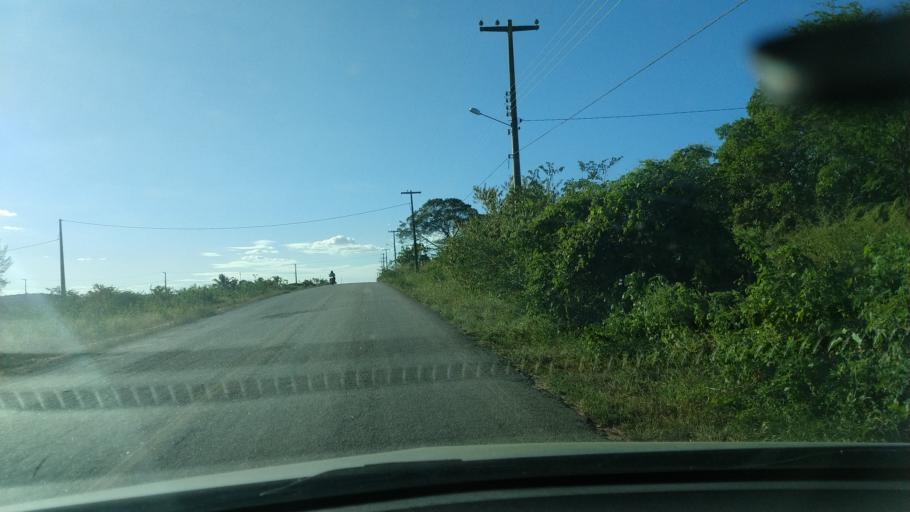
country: BR
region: Rio Grande do Norte
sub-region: Sao Jose Do Campestre
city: Sao Jose do Campestre
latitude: -6.4442
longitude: -35.6407
